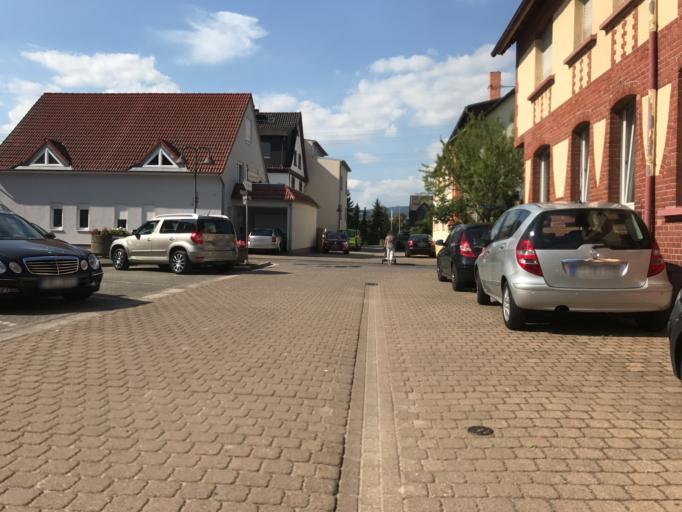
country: DE
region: Rheinland-Pfalz
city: Budenheim
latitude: 50.0262
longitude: 8.1701
